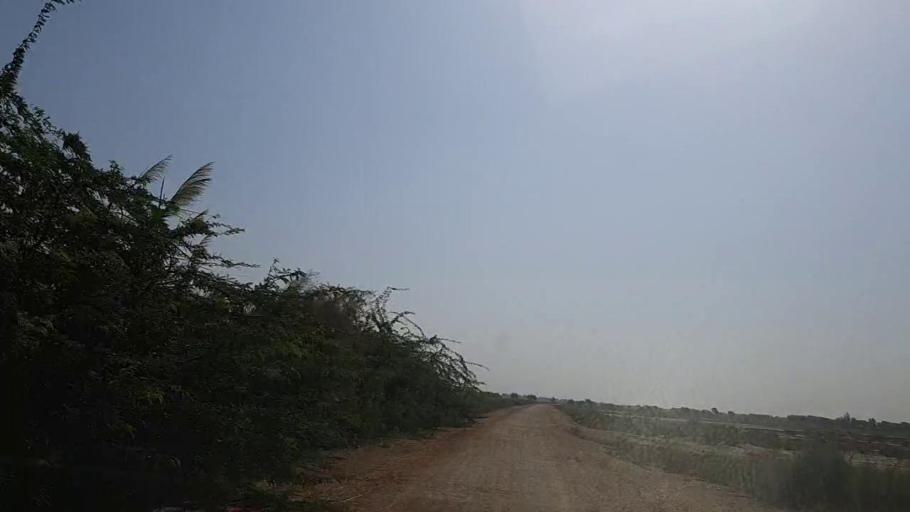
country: PK
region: Sindh
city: Daro Mehar
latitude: 24.7102
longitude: 68.1235
